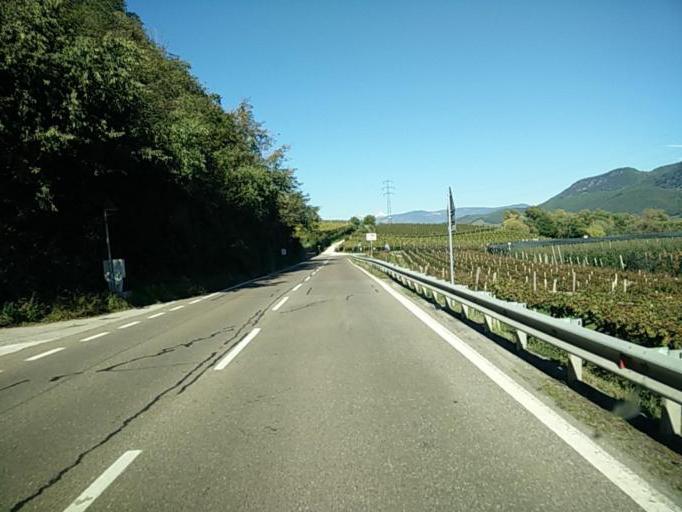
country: IT
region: Trentino-Alto Adige
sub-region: Bolzano
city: Termeno
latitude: 46.3677
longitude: 11.2511
